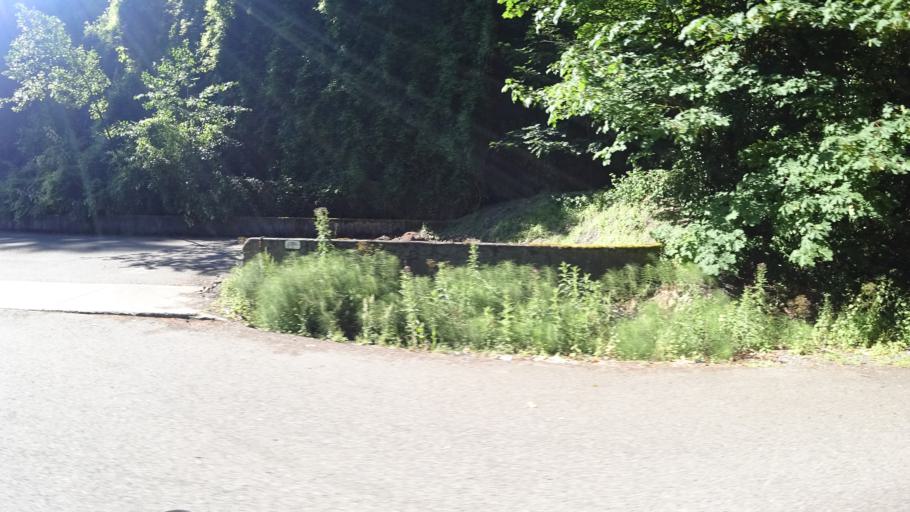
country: US
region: Oregon
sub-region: Multnomah County
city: Portland
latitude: 45.5230
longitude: -122.7124
